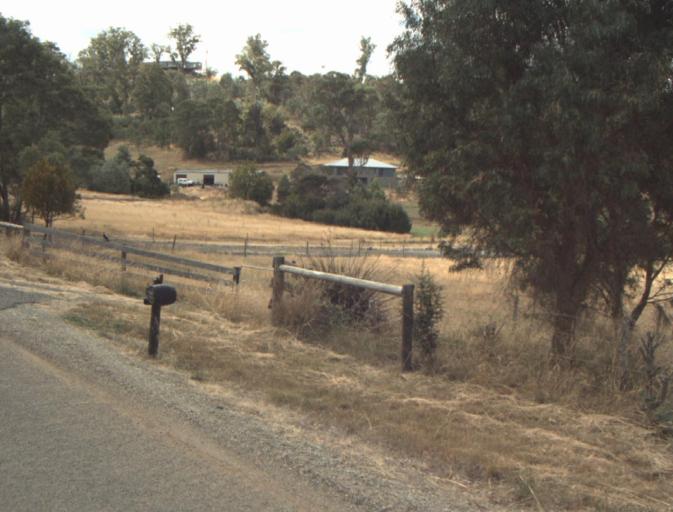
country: AU
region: Tasmania
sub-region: Launceston
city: Mayfield
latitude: -41.3045
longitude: 147.0459
